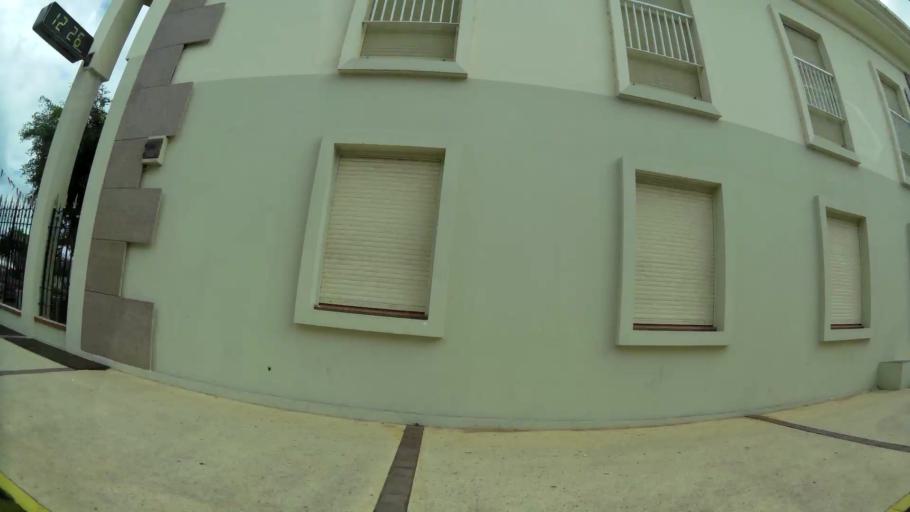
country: GP
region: Guadeloupe
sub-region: Guadeloupe
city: Baie-Mahault
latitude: 16.2678
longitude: -61.5872
